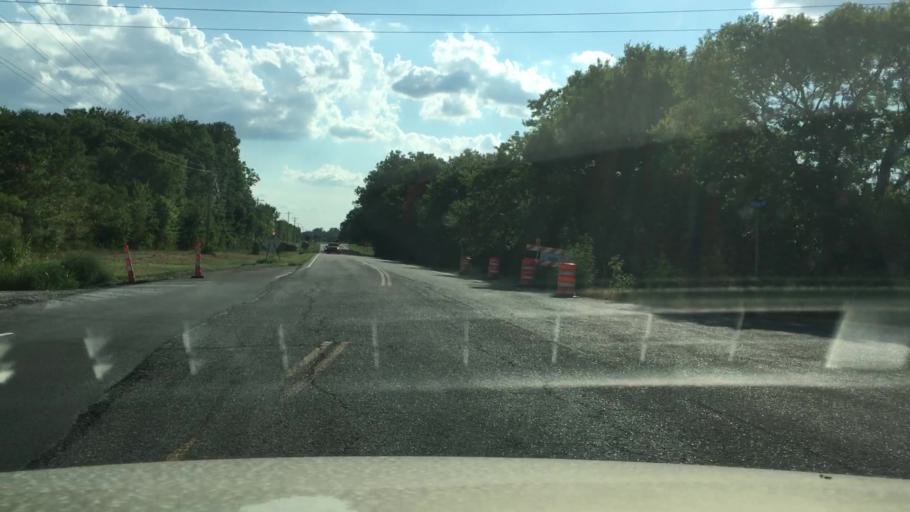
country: US
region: Oklahoma
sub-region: Cherokee County
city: Tahlequah
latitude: 35.9181
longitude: -95.0470
